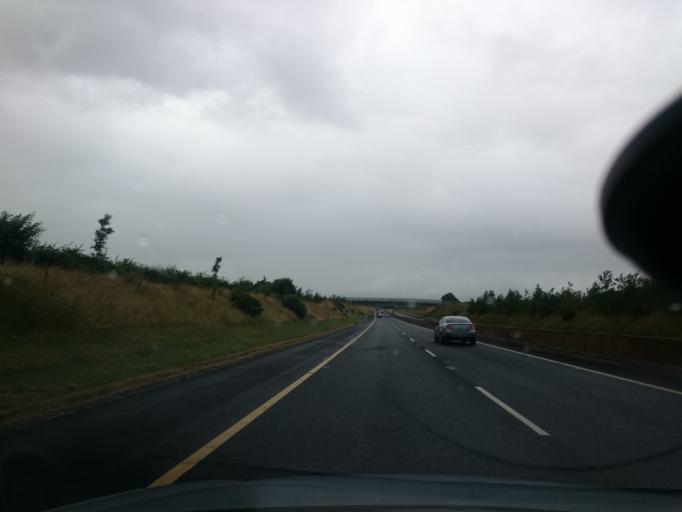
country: IE
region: Leinster
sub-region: Kildare
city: Castledermot
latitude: 52.9123
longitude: -6.8649
